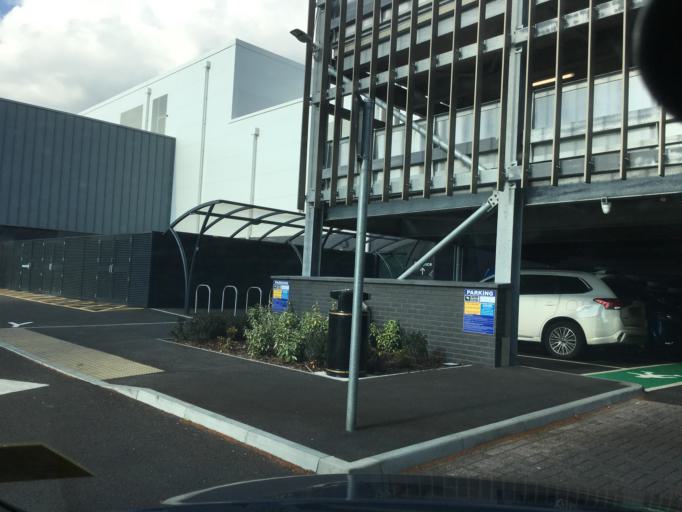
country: GB
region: England
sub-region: Surrey
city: Camberley
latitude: 51.3374
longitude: -0.7520
